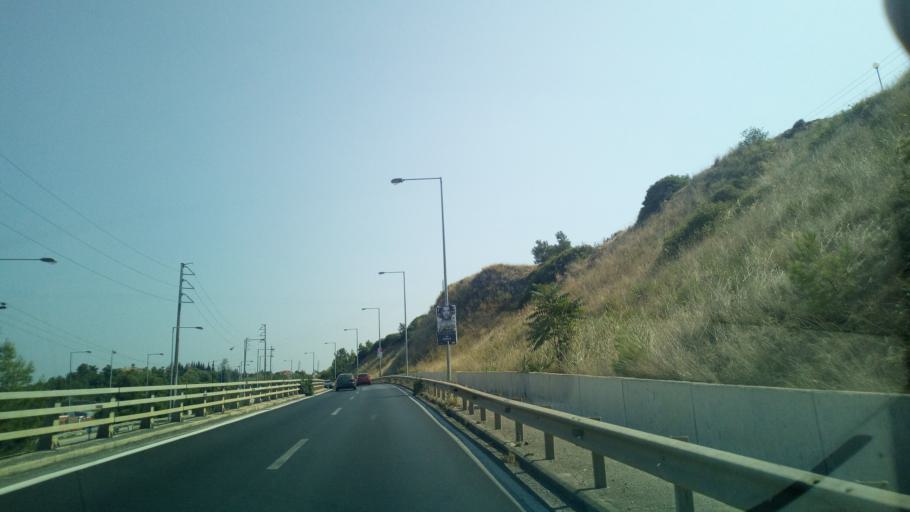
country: GR
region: Central Macedonia
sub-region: Nomos Chalkidikis
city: Nea Potidhaia
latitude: 40.1939
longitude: 23.3316
